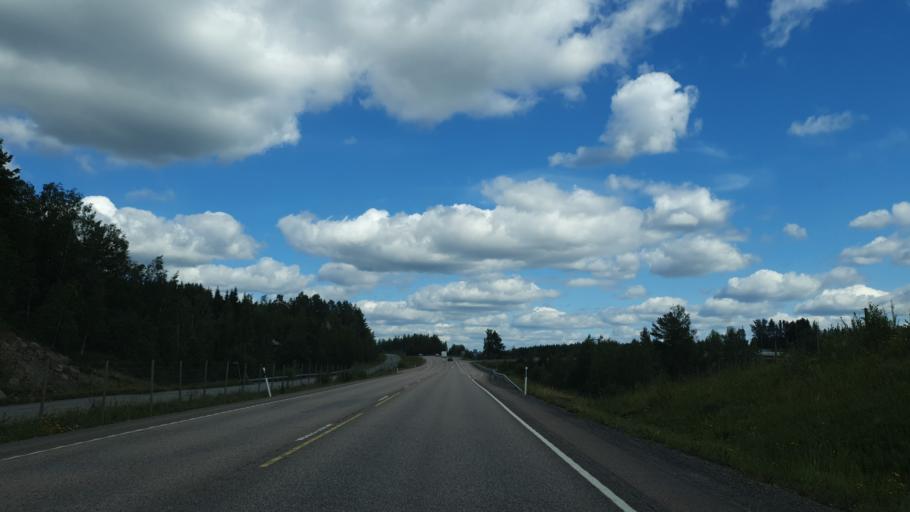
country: FI
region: Pirkanmaa
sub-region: Tampere
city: Kuhmalahti
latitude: 61.7142
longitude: 24.6381
